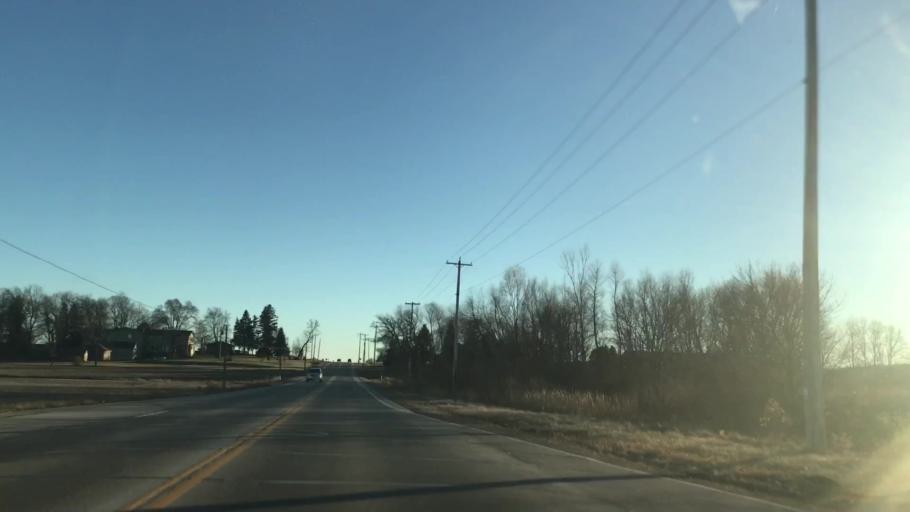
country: US
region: Wisconsin
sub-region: Washington County
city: Jackson
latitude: 43.2910
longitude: -88.1816
